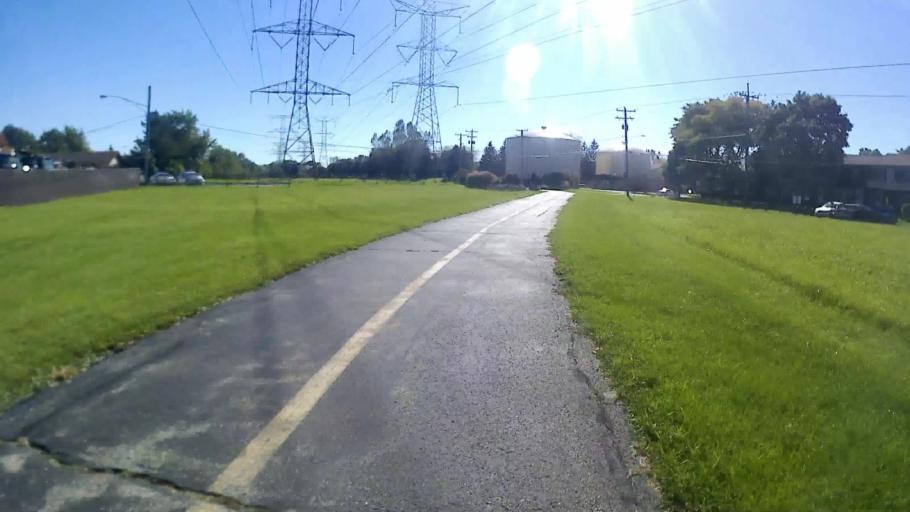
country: US
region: Illinois
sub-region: DuPage County
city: Wood Dale
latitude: 41.9614
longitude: -87.9937
